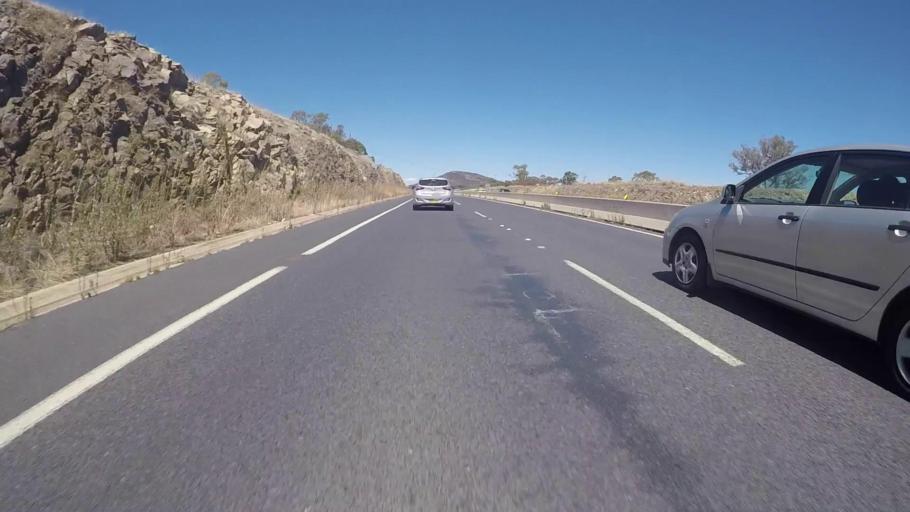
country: AU
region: Australian Capital Territory
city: Forrest
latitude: -35.3378
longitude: 149.0650
